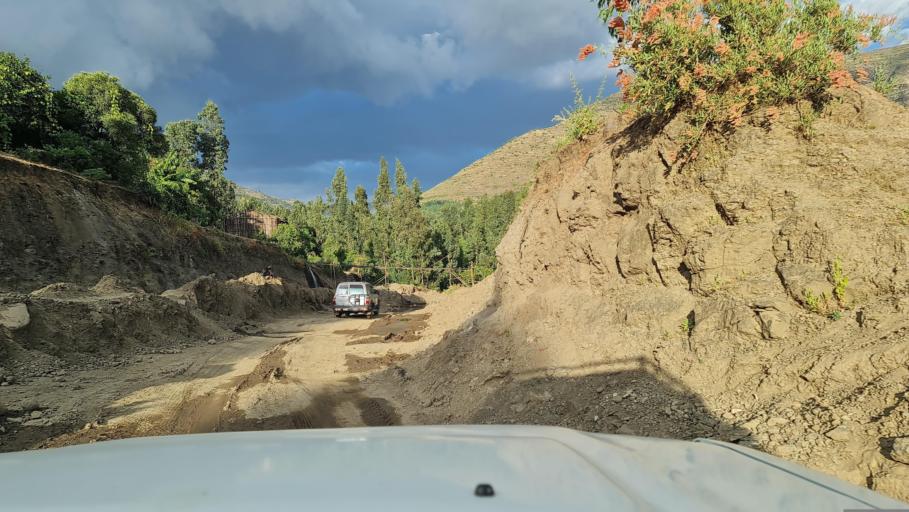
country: ET
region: Amhara
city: Debark'
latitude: 13.0412
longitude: 38.0534
